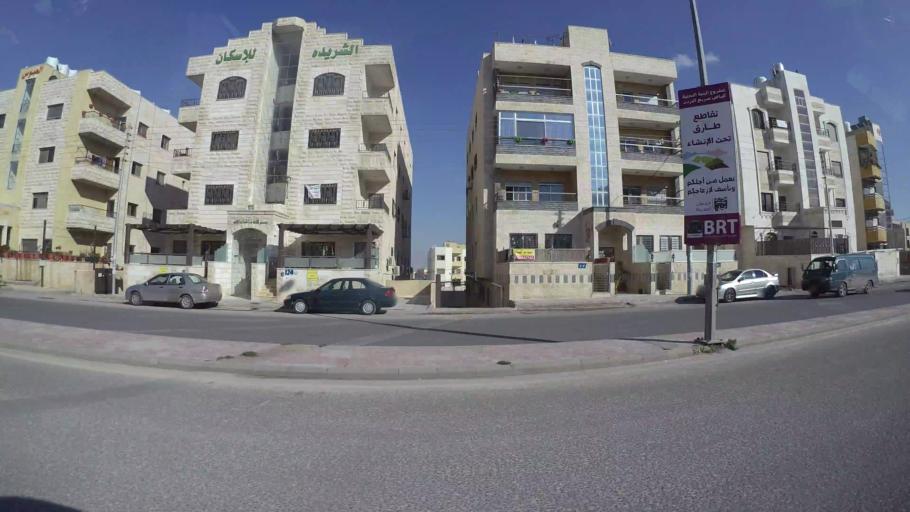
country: JO
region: Amman
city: Amman
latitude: 31.9870
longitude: 35.9431
